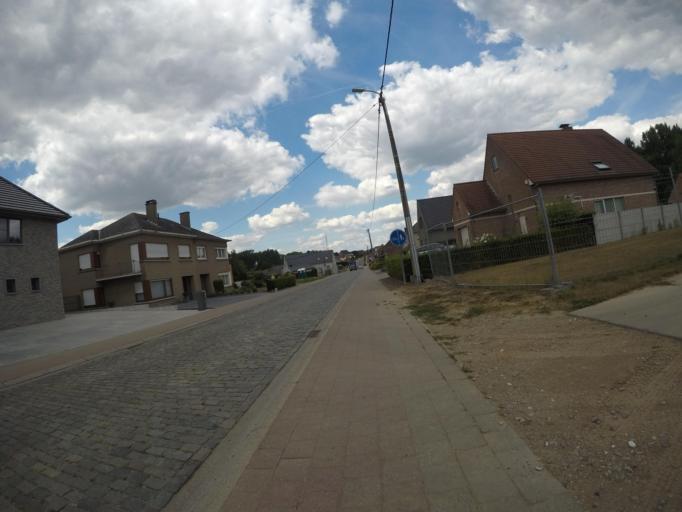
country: BE
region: Flanders
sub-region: Provincie Vlaams-Brabant
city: Ledeberg
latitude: 50.8503
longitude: 4.0840
